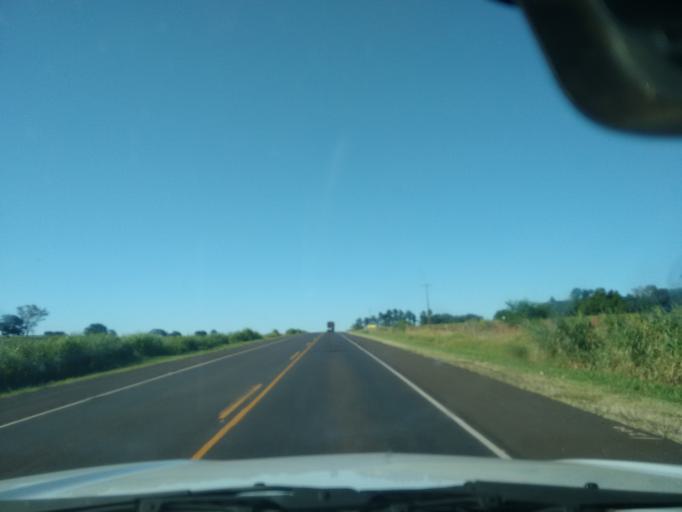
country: PY
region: Canindeyu
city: Salto del Guaira
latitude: -23.9773
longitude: -54.3310
